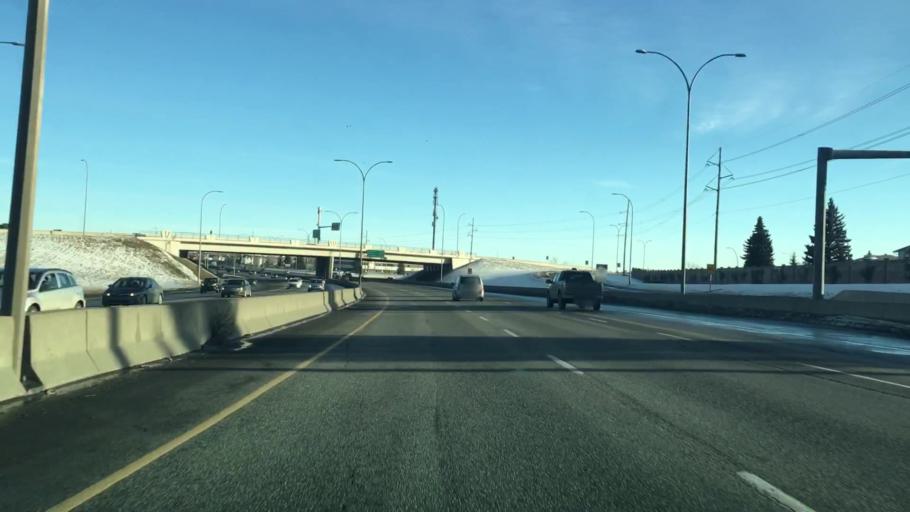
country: CA
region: Alberta
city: Calgary
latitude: 50.9818
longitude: -114.0185
